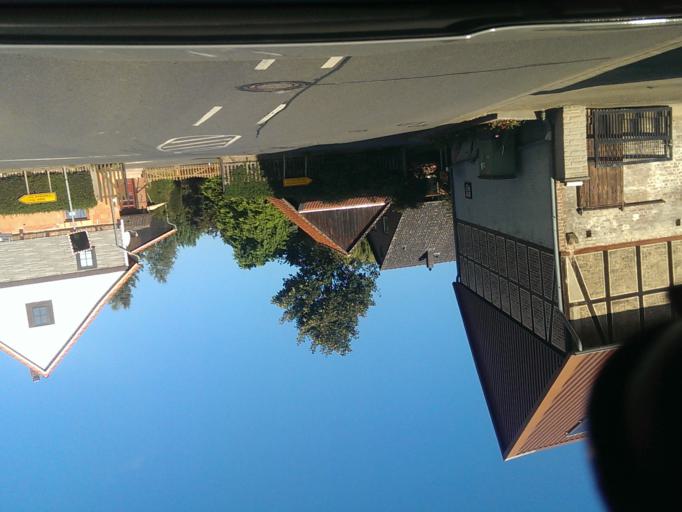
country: DE
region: Lower Saxony
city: Vienenburg
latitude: 51.9318
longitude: 10.5939
